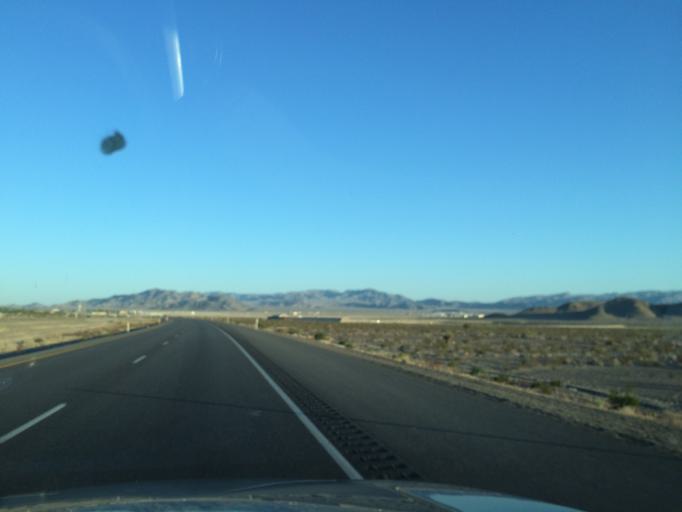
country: US
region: Nevada
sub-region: Nye County
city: Pahrump
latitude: 36.5755
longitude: -115.6401
